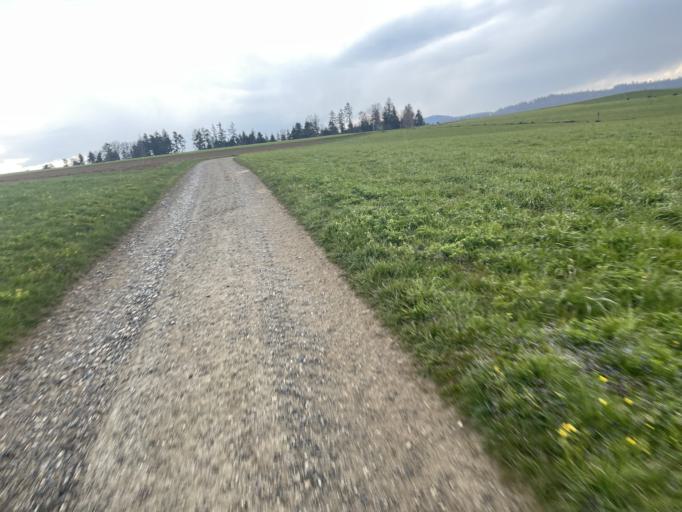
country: CH
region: Bern
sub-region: Bern-Mittelland District
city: Taegertschi
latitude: 46.9046
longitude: 7.5956
